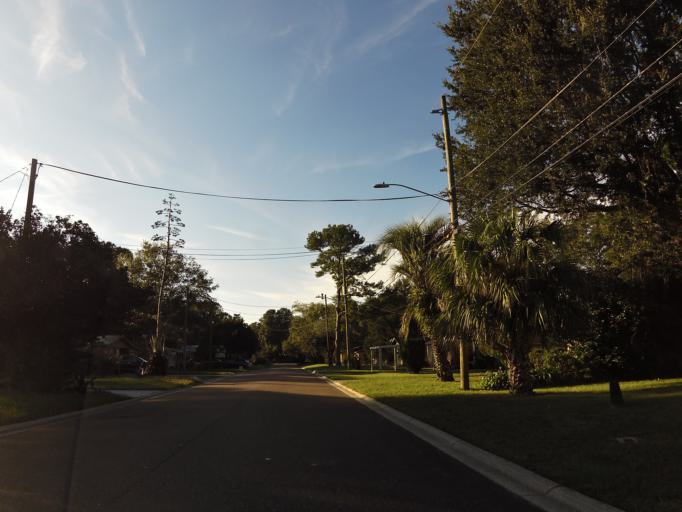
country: US
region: Florida
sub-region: Duval County
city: Jacksonville
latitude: 30.3551
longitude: -81.7064
